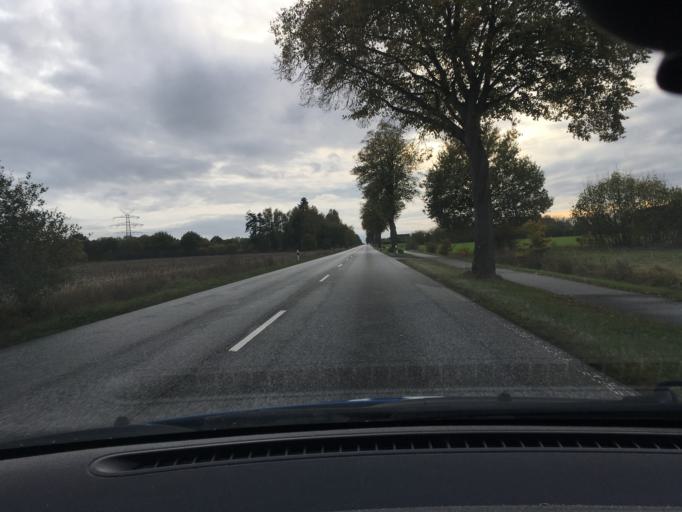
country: DE
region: Schleswig-Holstein
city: Grabau
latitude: 53.5250
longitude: 10.5097
